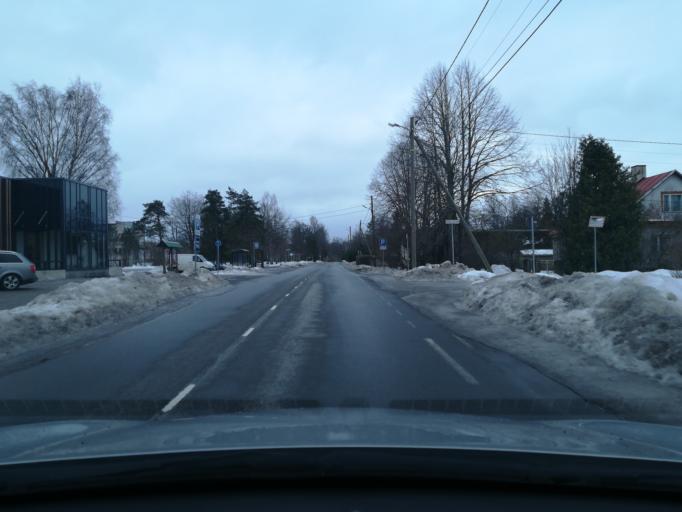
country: EE
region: Harju
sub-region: Nissi vald
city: Turba
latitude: 59.0807
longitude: 24.2361
